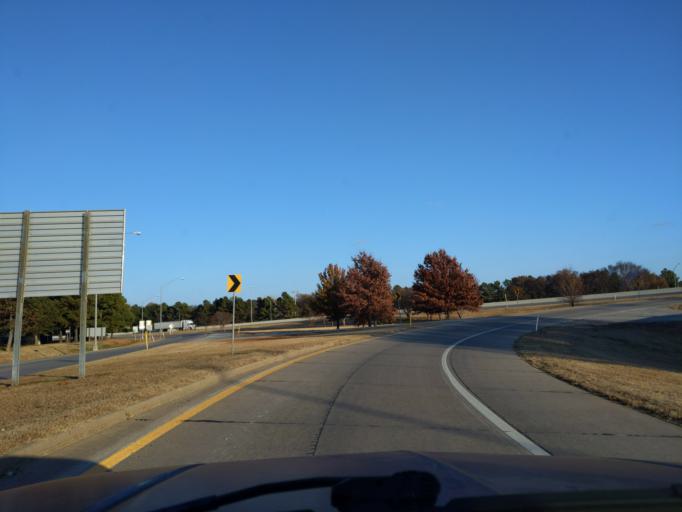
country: US
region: Oklahoma
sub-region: Tulsa County
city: Jenks
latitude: 36.0217
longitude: -95.9470
